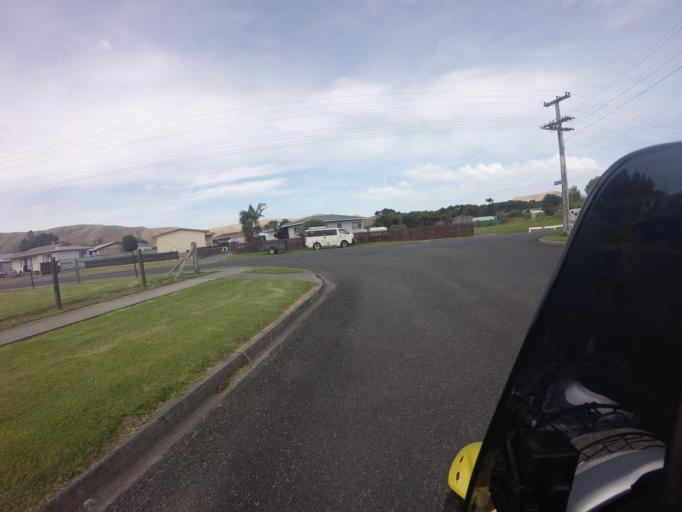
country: NZ
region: Gisborne
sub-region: Gisborne District
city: Gisborne
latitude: -38.6858
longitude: 178.0579
